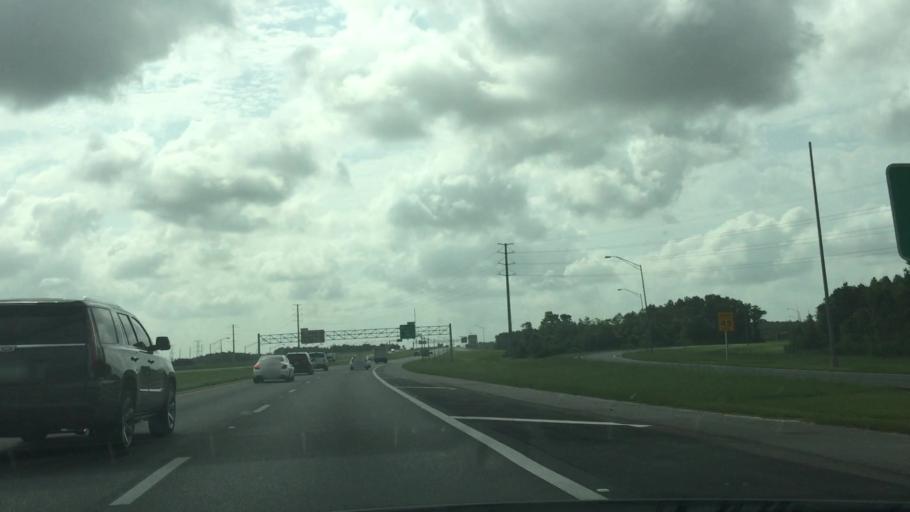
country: US
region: Florida
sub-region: Orange County
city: Hunters Creek
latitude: 28.3736
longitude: -81.4185
